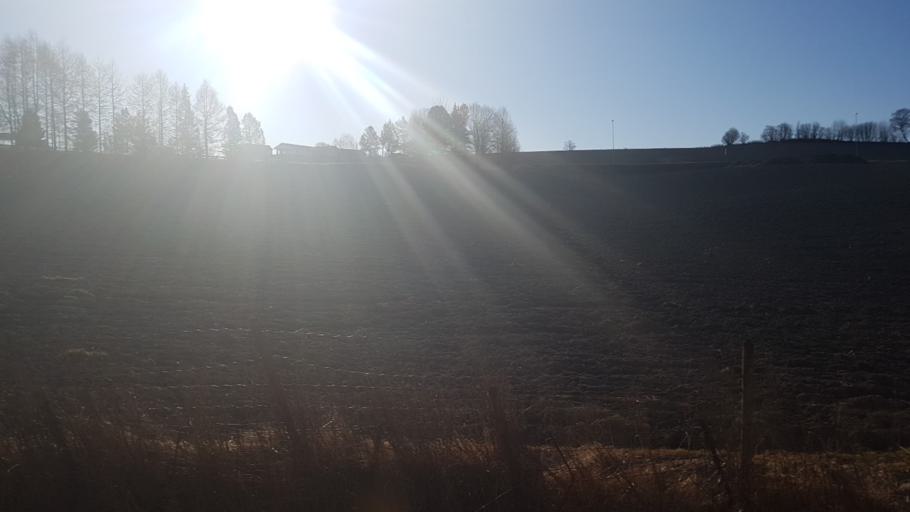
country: NO
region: Nord-Trondelag
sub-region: Levanger
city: Skogn
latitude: 63.6742
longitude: 11.0995
